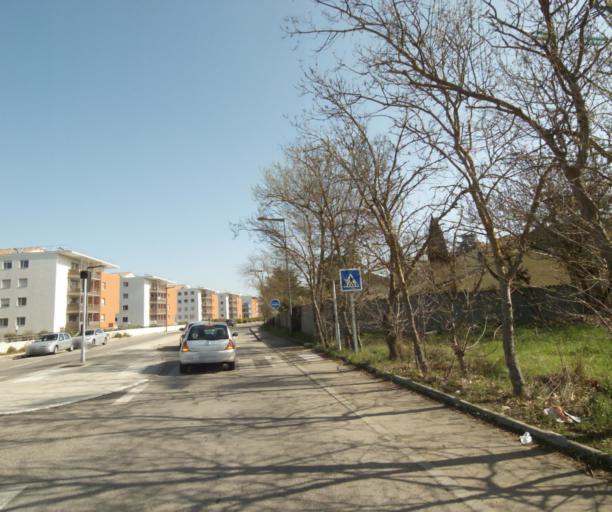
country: FR
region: Provence-Alpes-Cote d'Azur
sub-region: Departement des Bouches-du-Rhone
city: Aix-en-Provence
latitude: 43.5096
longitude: 5.4327
